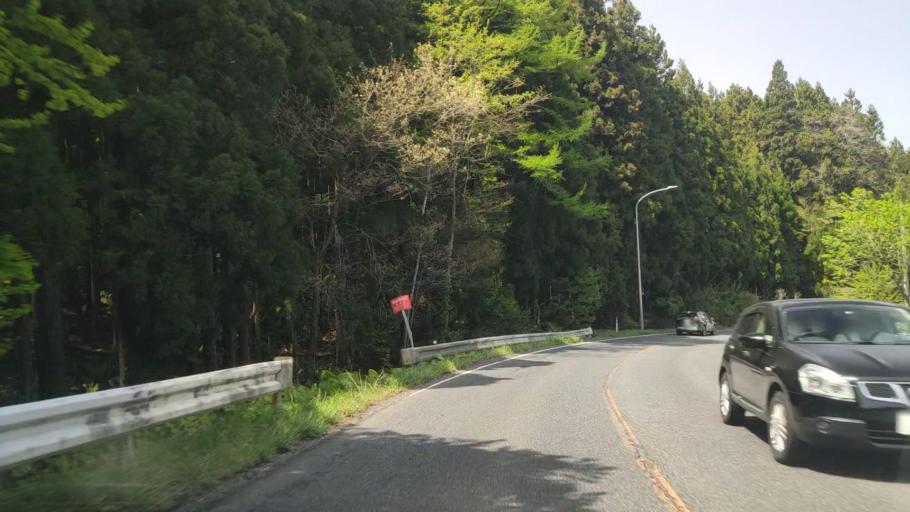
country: JP
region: Aomori
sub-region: Misawa Shi
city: Inuotose
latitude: 40.5833
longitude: 141.3570
